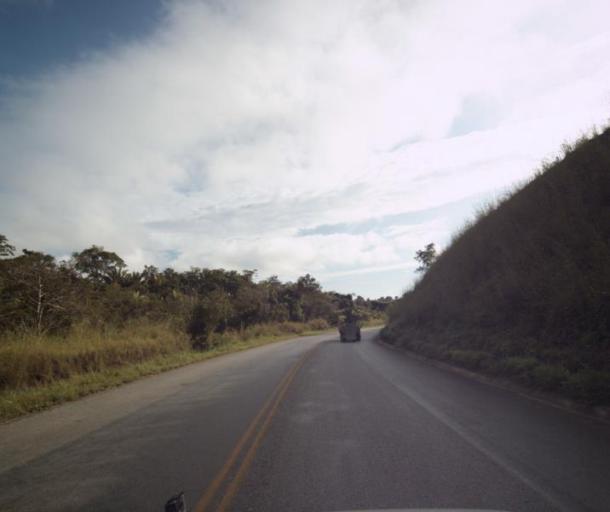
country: BR
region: Goias
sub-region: Pirenopolis
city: Pirenopolis
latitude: -15.7152
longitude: -48.6957
